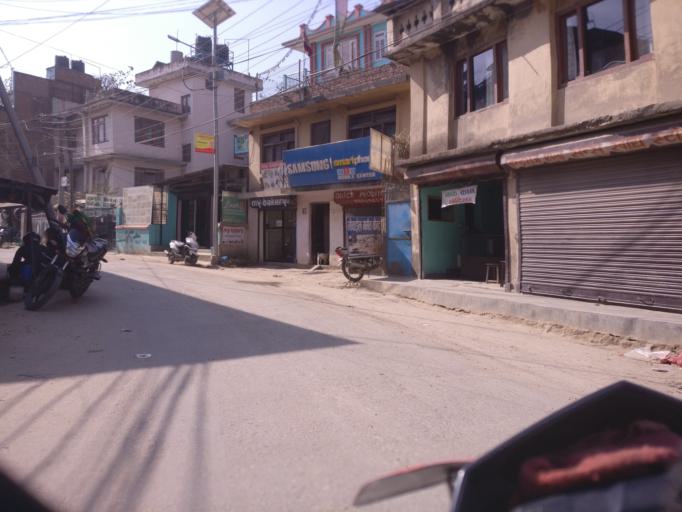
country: NP
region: Central Region
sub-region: Bagmati Zone
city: Patan
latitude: 27.6586
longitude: 85.3229
